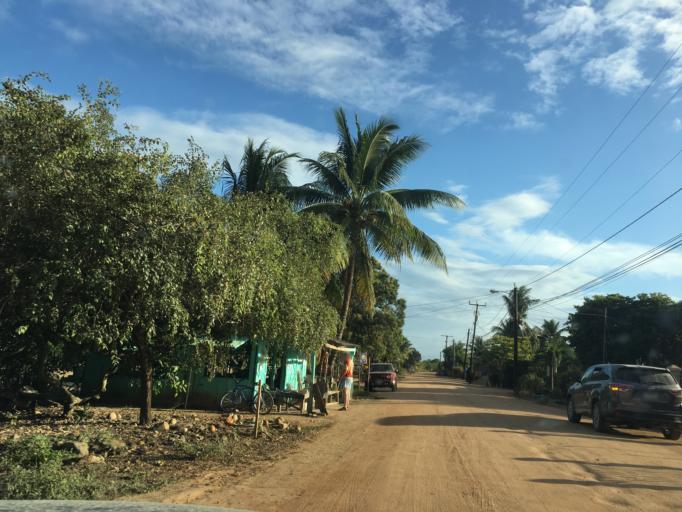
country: BZ
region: Stann Creek
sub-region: Dangriga
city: Dangriga
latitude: 16.8533
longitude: -88.2801
